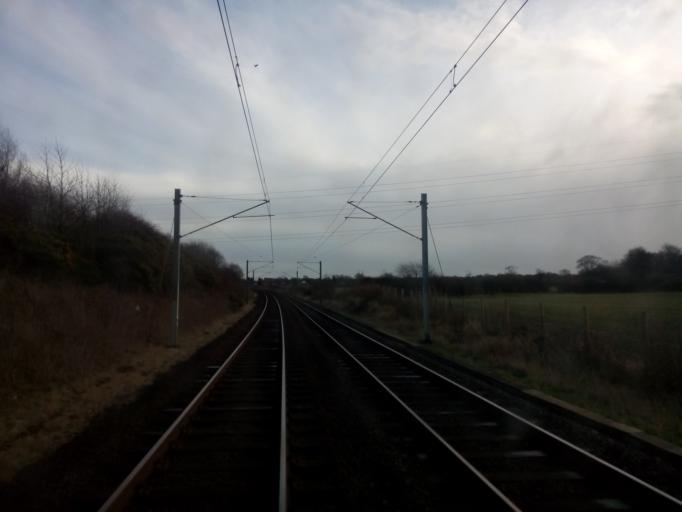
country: GB
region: England
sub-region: Newcastle upon Tyne
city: Dinnington
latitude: 55.0182
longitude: -1.6906
